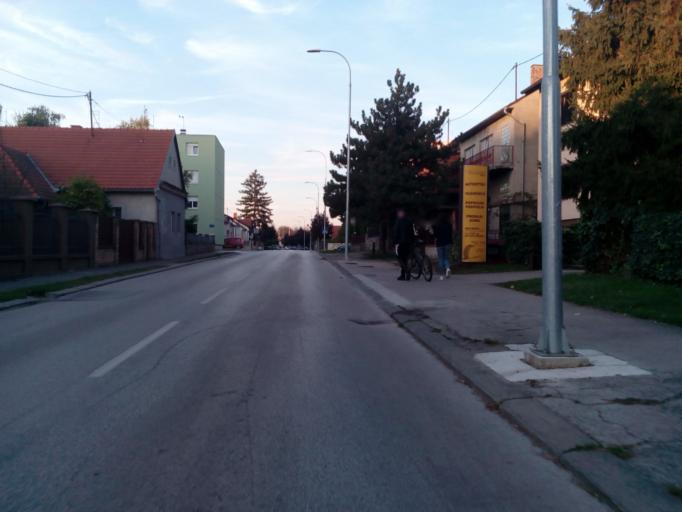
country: HR
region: Vukovarsko-Srijemska
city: Vinkovci
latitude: 45.2955
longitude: 18.8149
